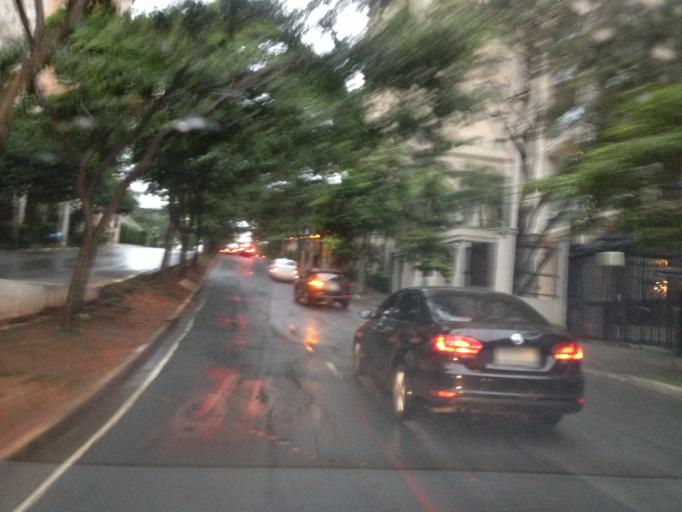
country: BR
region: Sao Paulo
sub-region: Sao Paulo
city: Sao Paulo
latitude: -23.5973
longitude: -46.6648
